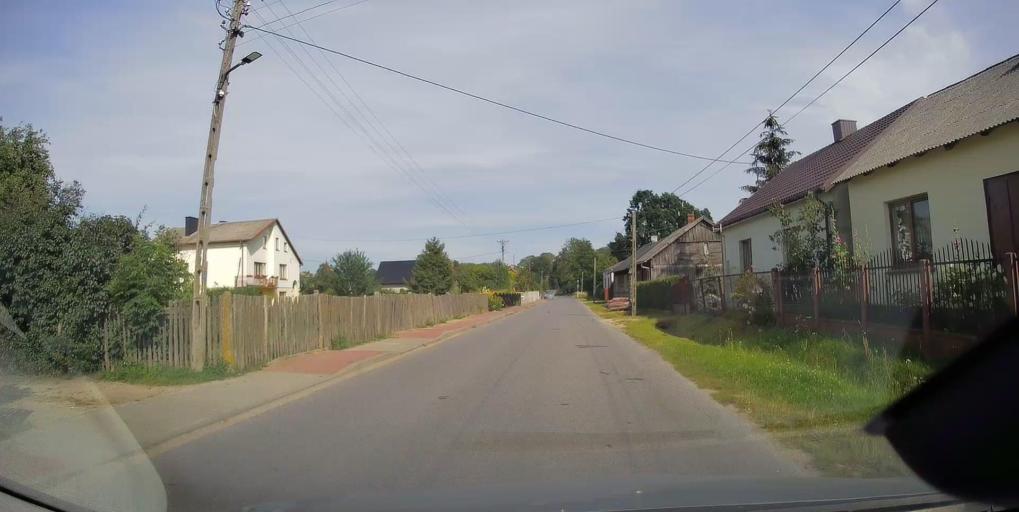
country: PL
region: Lodz Voivodeship
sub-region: Powiat opoczynski
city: Mniszkow
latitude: 51.4112
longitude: 20.0406
